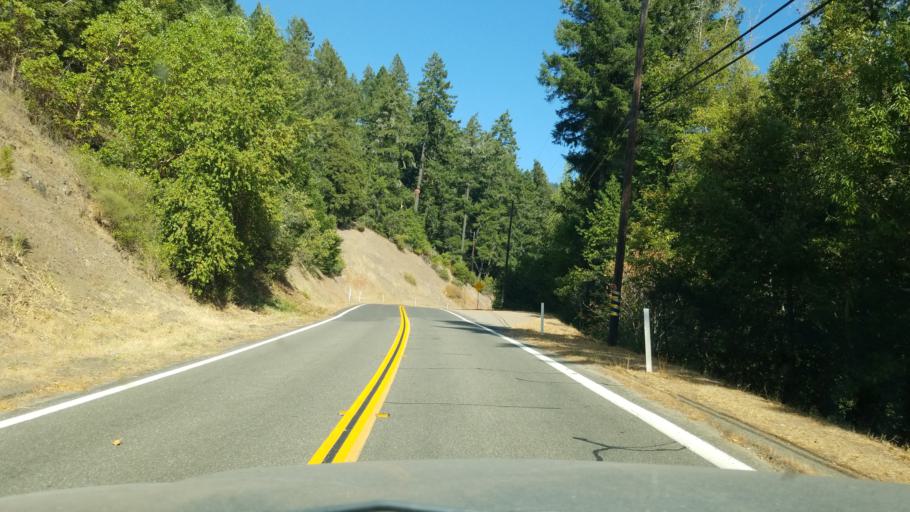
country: US
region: California
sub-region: Humboldt County
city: Redway
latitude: 40.2217
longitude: -123.7952
